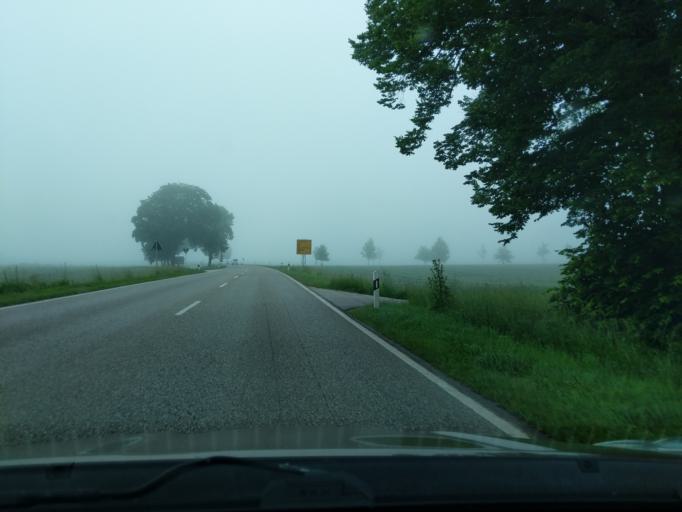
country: DE
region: Bavaria
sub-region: Swabia
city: Gessertshausen
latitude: 48.3371
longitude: 10.7502
